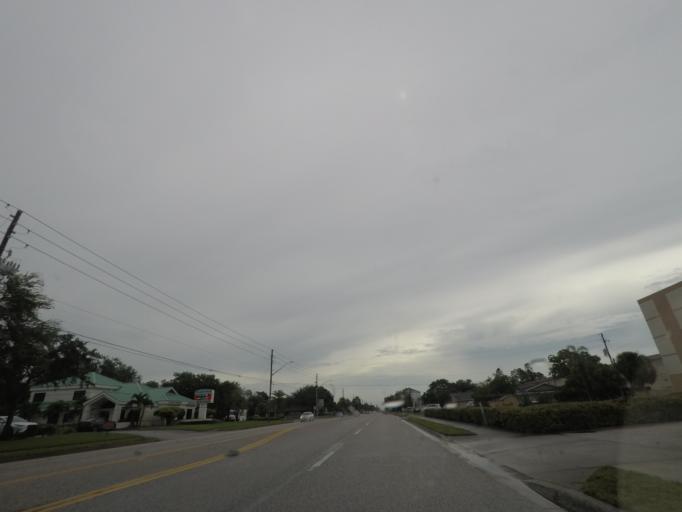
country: US
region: Florida
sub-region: Pinellas County
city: Kenneth City
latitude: 27.8063
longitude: -82.7452
